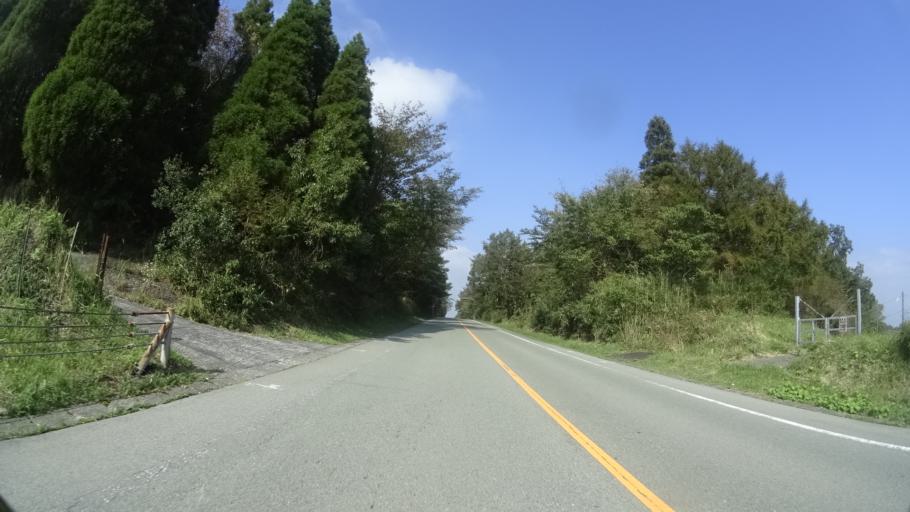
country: JP
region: Kumamoto
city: Aso
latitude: 33.0298
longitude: 131.0633
